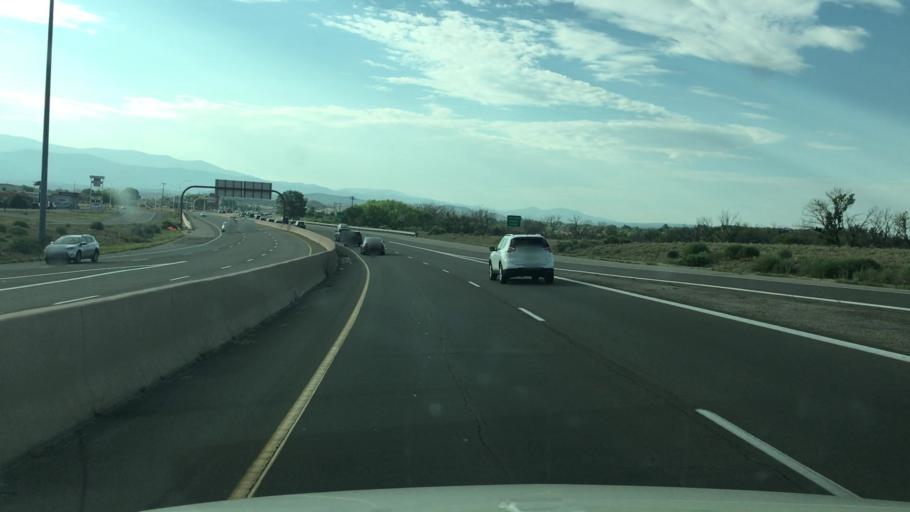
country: US
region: New Mexico
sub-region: Santa Fe County
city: Pojoaque
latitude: 35.8884
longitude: -106.0215
